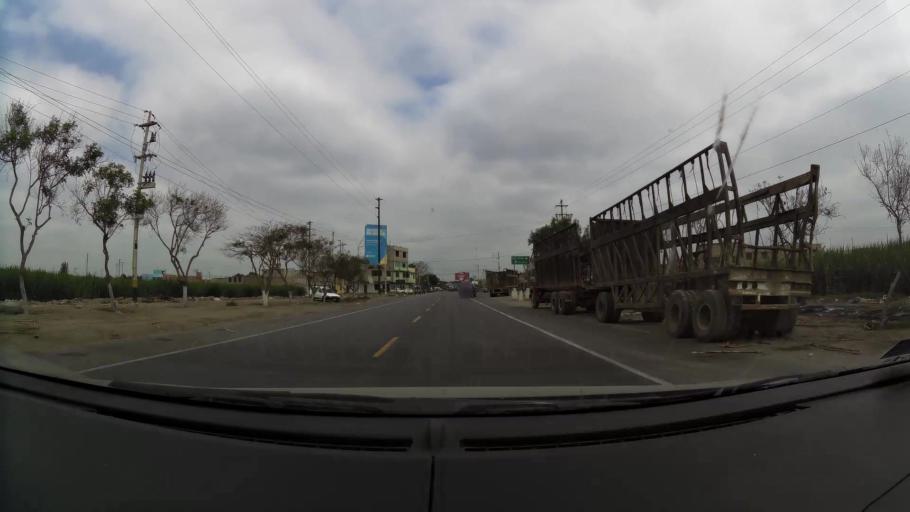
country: PE
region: La Libertad
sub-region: Ascope
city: Chocope
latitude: -7.7930
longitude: -79.2177
